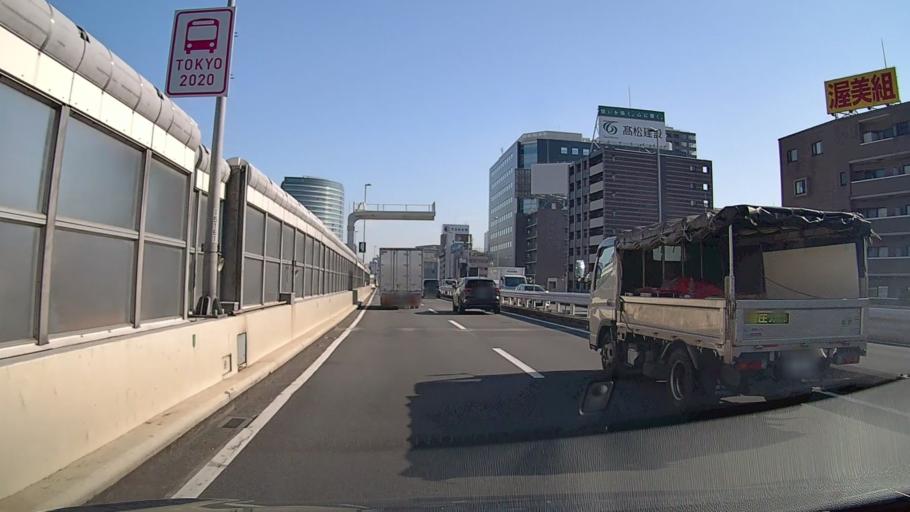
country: JP
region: Tokyo
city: Tokyo
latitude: 35.7093
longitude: 139.7352
